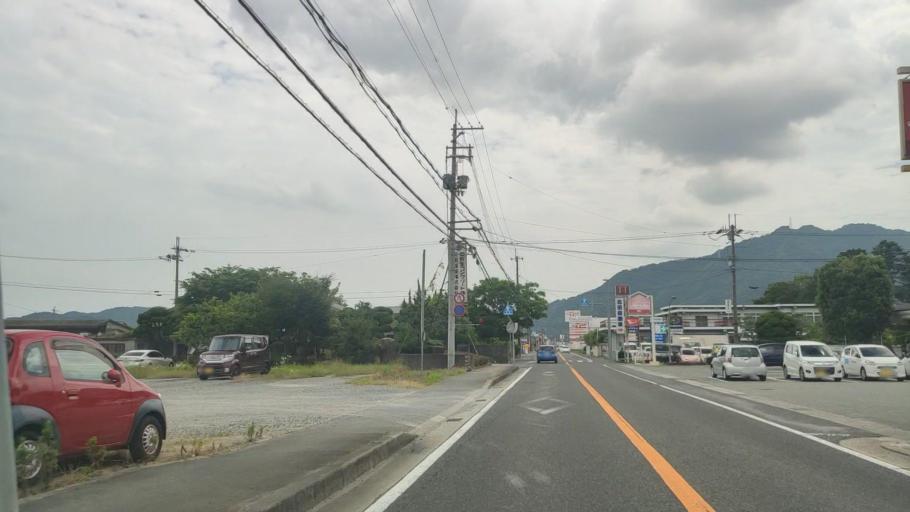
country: JP
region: Hyogo
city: Tatsunocho-tominaga
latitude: 34.9035
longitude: 134.5481
